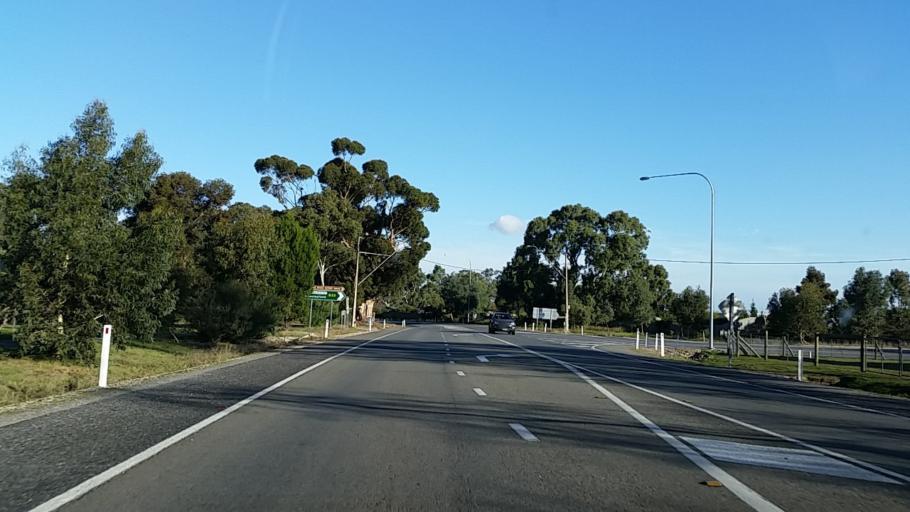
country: AU
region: South Australia
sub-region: Alexandrina
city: Strathalbyn
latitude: -35.2420
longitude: 138.8941
